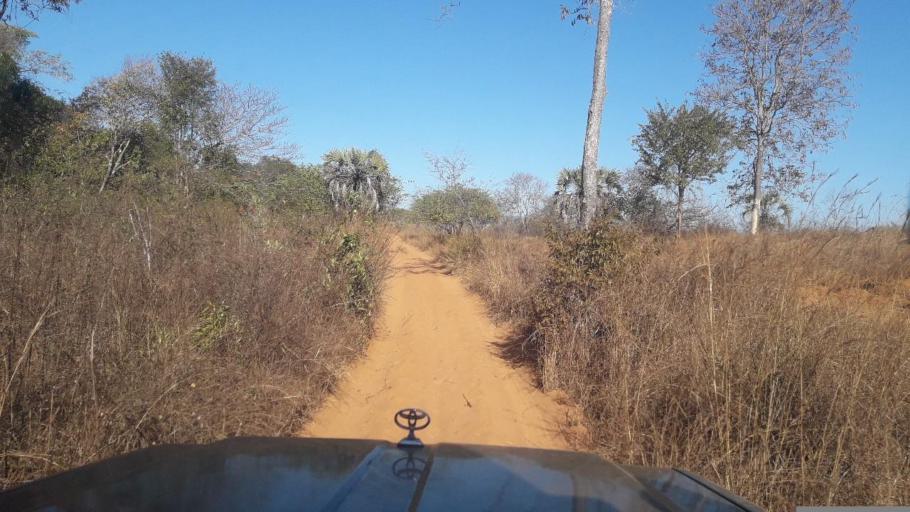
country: MG
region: Boeny
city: Sitampiky
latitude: -16.4148
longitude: 45.6060
